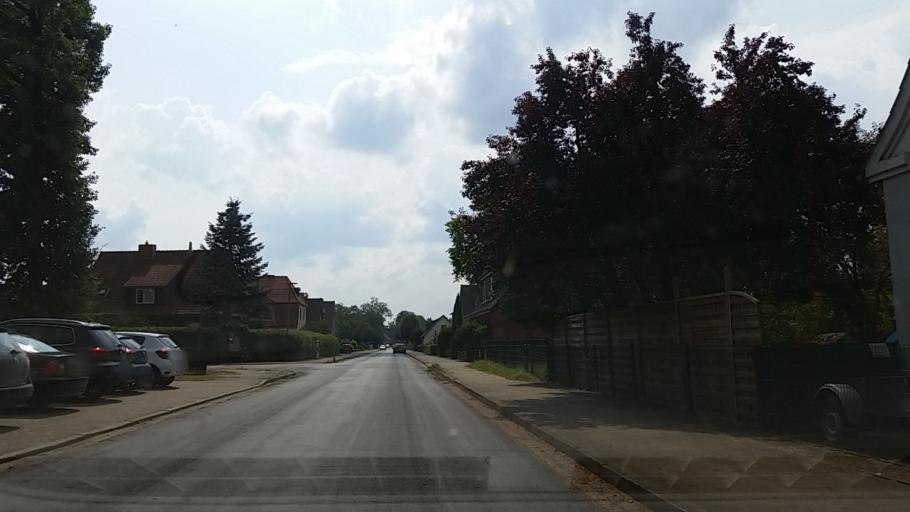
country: DE
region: Lower Saxony
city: Schneverdingen
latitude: 53.1256
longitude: 9.7854
